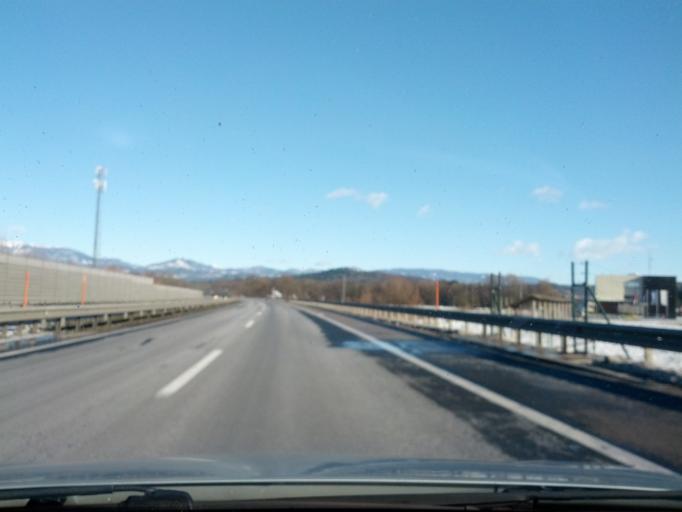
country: SI
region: Dol pri Ljubljani
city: Dol pri Ljubljani
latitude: 46.1039
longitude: 14.5967
